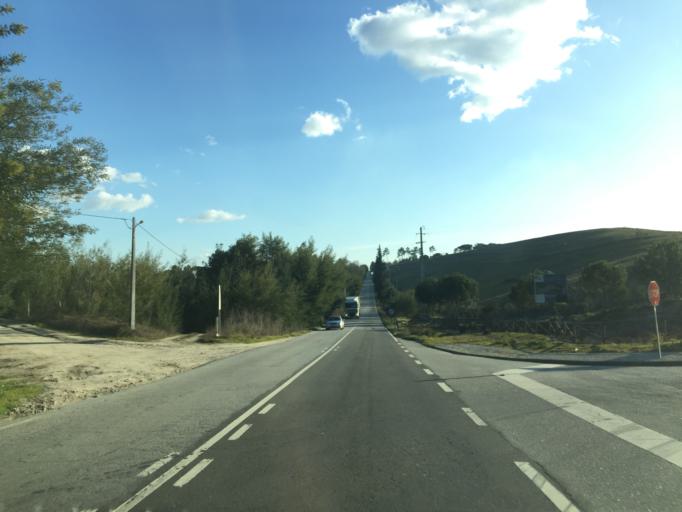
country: PT
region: Viseu
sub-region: Nelas
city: Nelas
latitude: 40.5123
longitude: -7.8890
